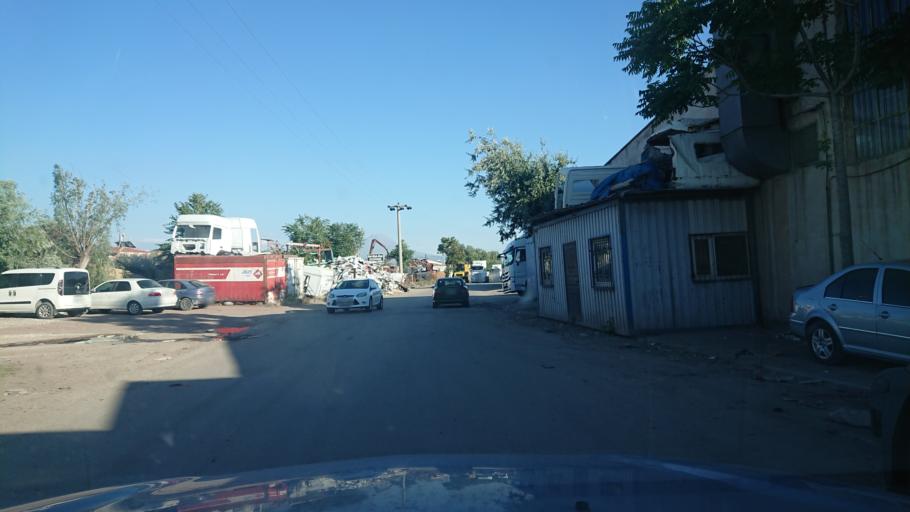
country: TR
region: Aksaray
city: Aksaray
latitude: 38.3760
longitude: 33.9914
